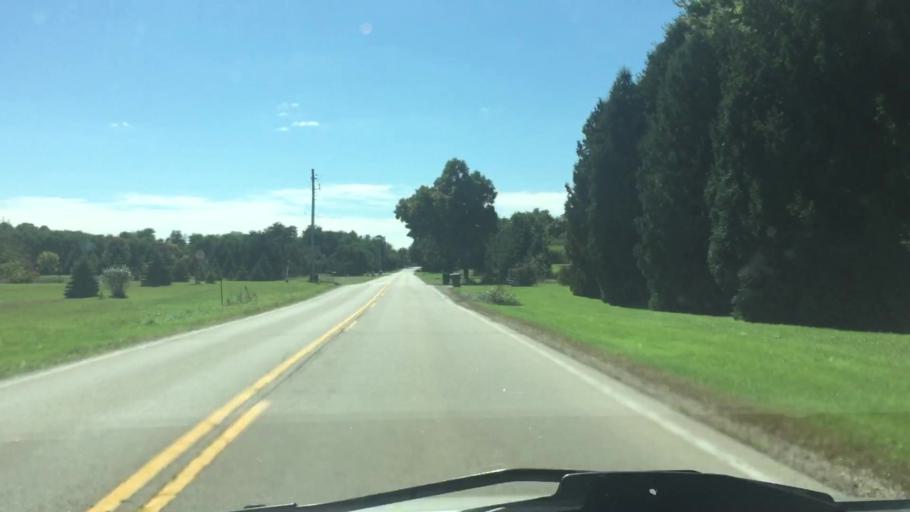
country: US
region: Wisconsin
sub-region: Waukesha County
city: North Prairie
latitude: 42.9624
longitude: -88.4049
